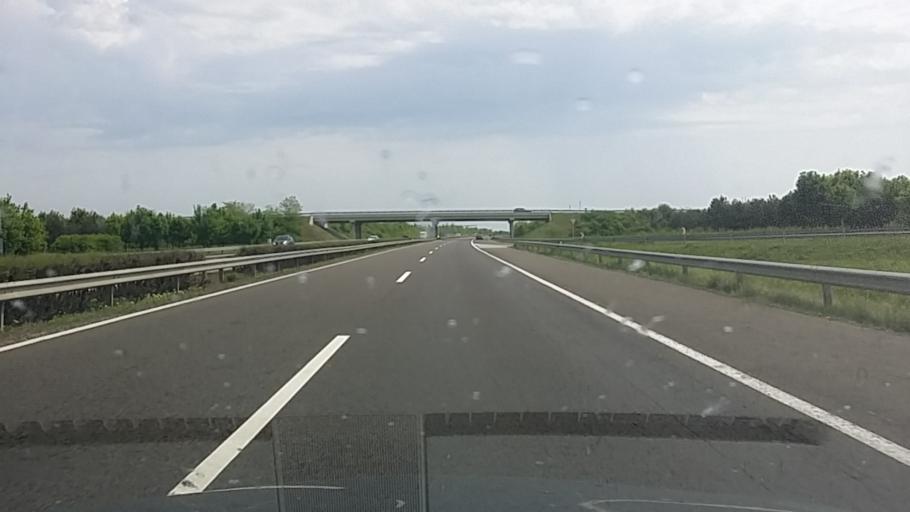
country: HU
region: Heves
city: Gyongyoshalasz
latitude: 47.7324
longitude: 19.9564
